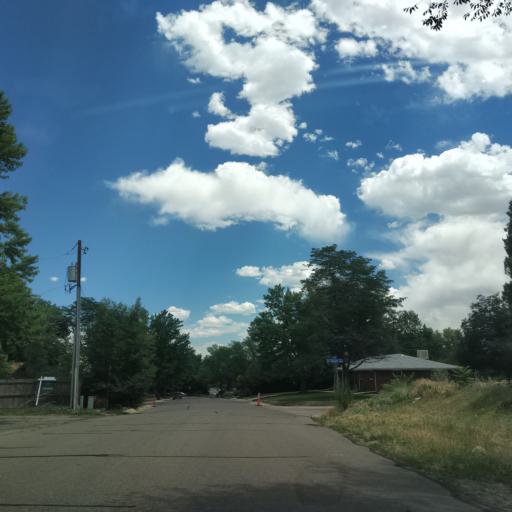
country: US
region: Colorado
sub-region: Jefferson County
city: Lakewood
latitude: 39.6860
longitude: -105.0889
